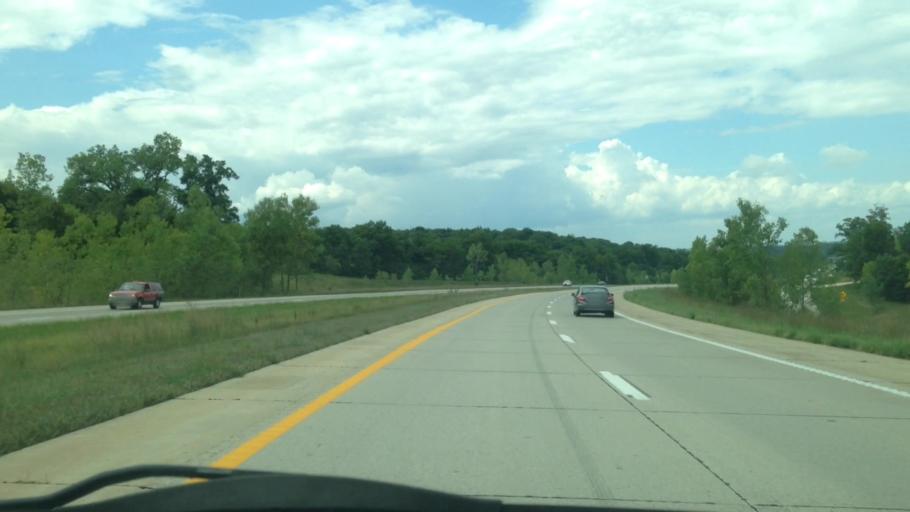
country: US
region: Missouri
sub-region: Pike County
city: Bowling Green
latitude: 39.3965
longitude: -91.2406
